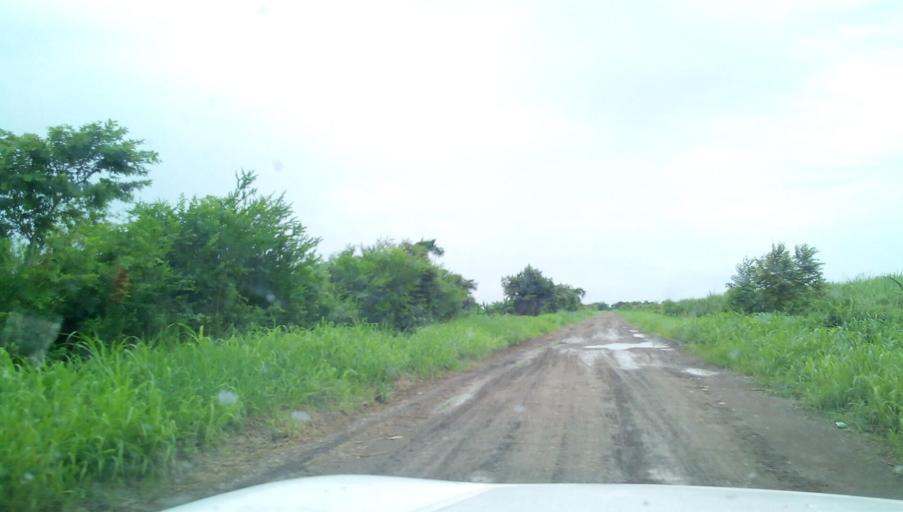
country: MX
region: Veracruz
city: Panuco
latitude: 21.8400
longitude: -98.1103
